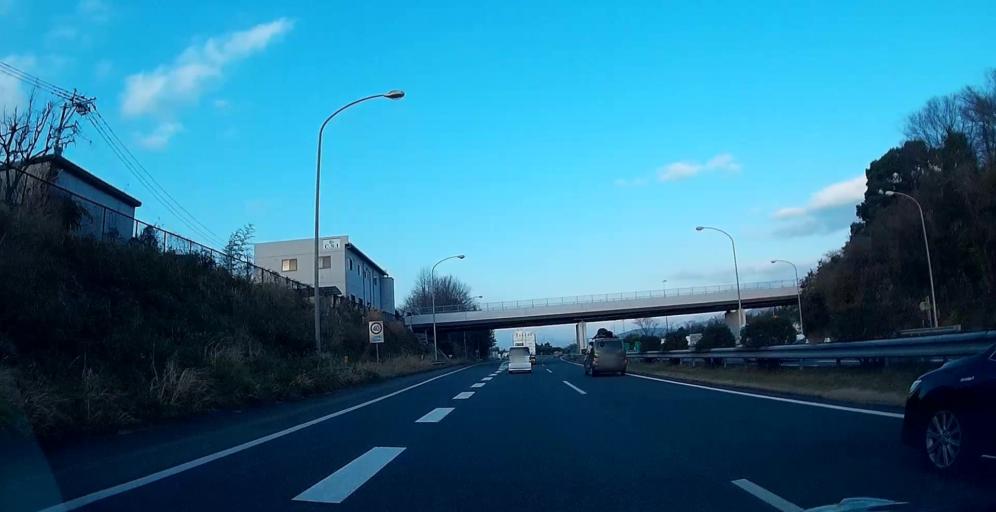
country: JP
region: Kumamoto
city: Uto
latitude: 32.7071
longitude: 130.7551
